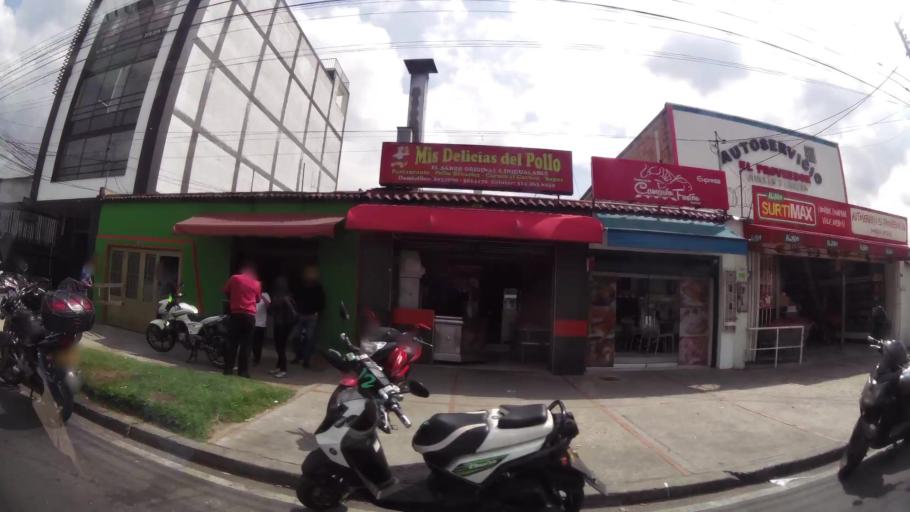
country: CO
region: Bogota D.C.
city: Bogota
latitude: 4.6052
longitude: -74.1142
